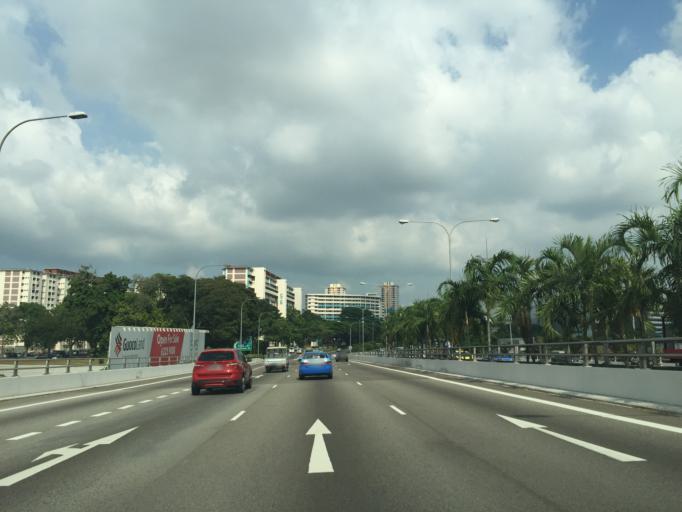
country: SG
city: Singapore
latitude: 1.3206
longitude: 103.8810
